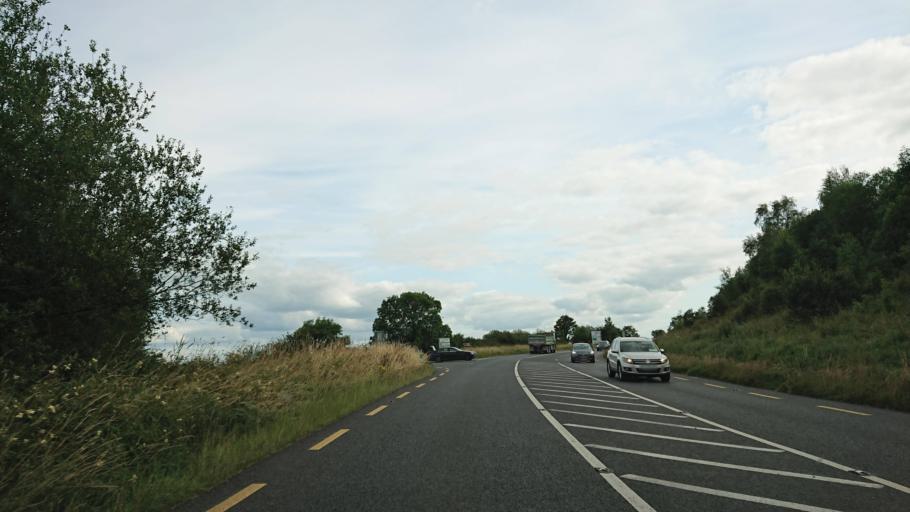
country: IE
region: Connaught
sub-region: County Leitrim
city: Carrick-on-Shannon
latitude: 53.9771
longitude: -8.0601
